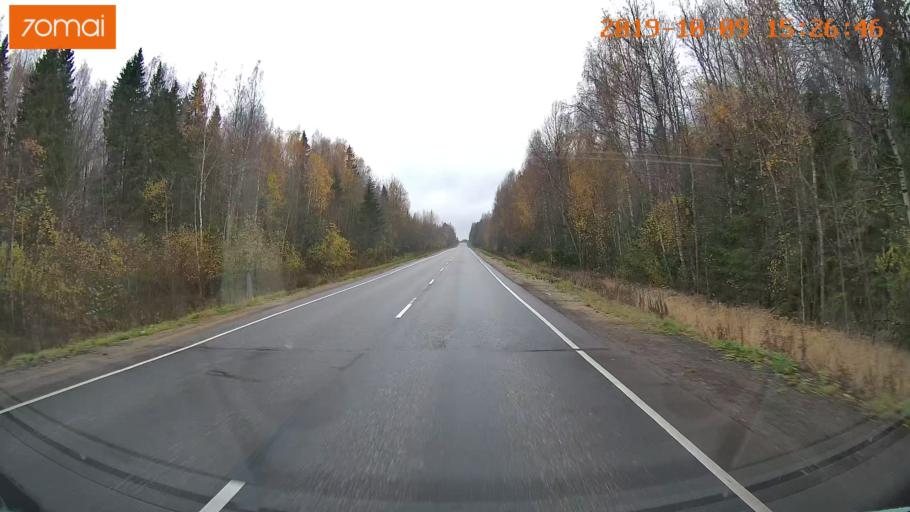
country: RU
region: Kostroma
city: Susanino
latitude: 58.0177
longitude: 41.3955
